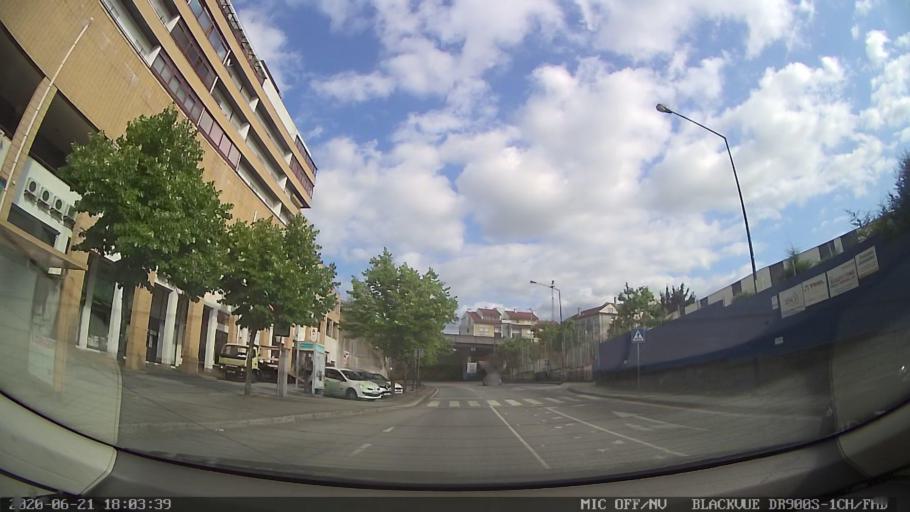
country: PT
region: Porto
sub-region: Amarante
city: Amarante
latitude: 41.2717
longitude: -8.0805
